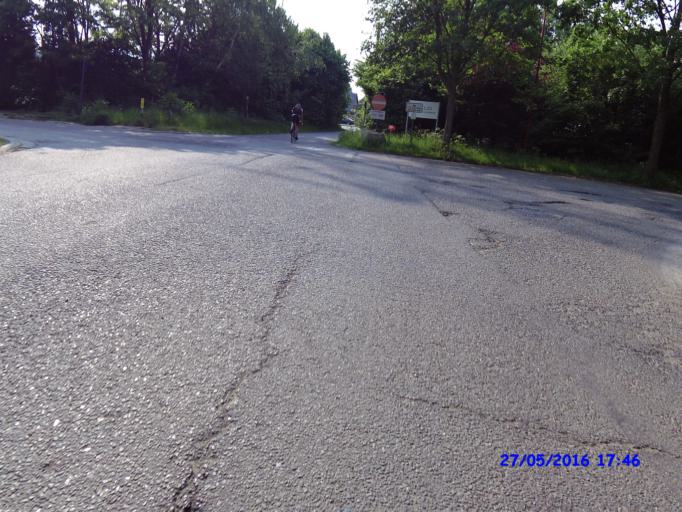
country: BE
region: Flanders
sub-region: Provincie Vlaams-Brabant
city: Asse
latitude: 50.8975
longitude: 4.2457
